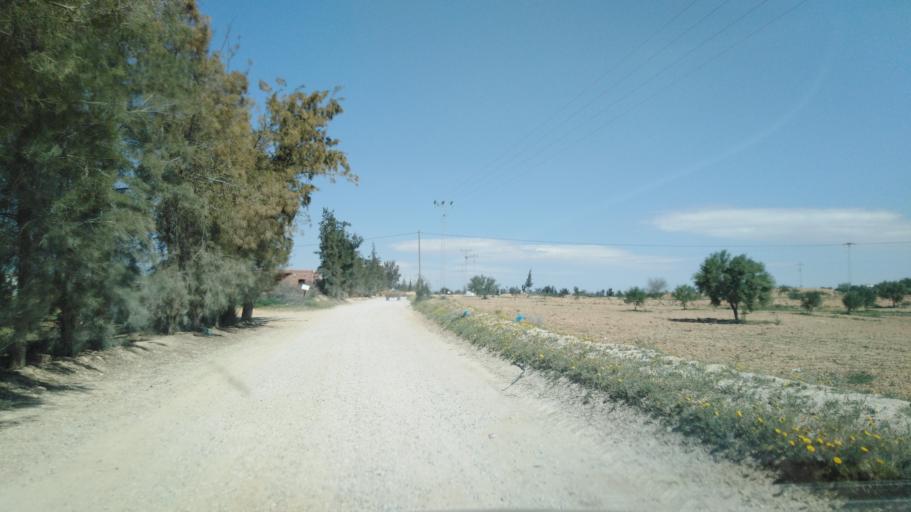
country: TN
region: Safaqis
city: Sfax
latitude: 34.7572
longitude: 10.5293
